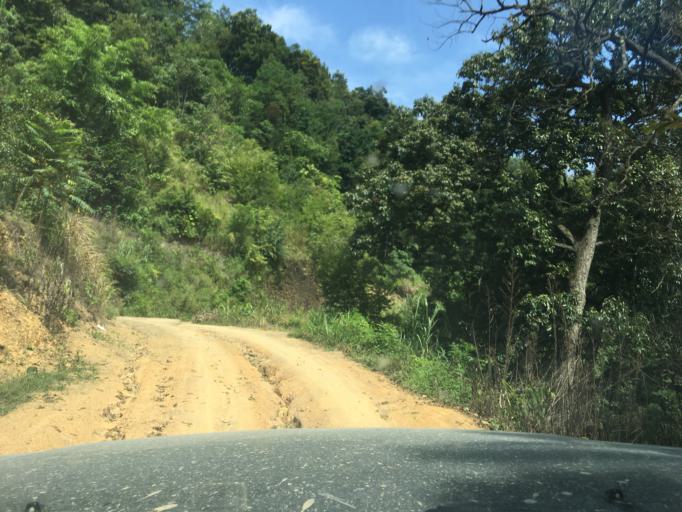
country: CN
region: Guangxi Zhuangzu Zizhiqu
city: Xinzhou
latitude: 25.0461
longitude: 105.8605
